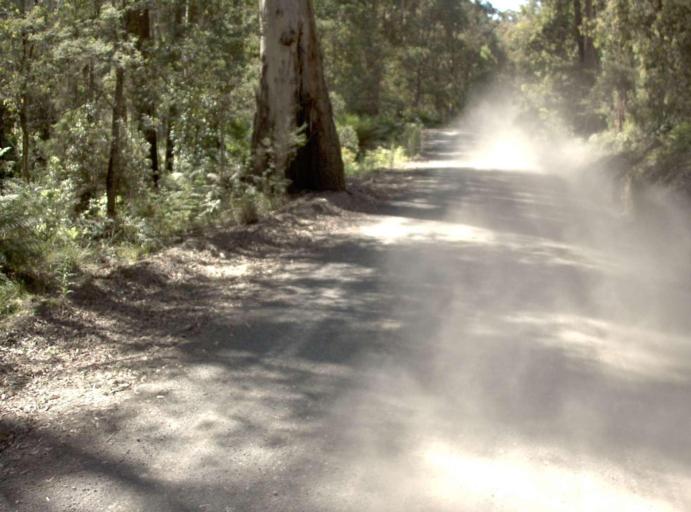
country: AU
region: New South Wales
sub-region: Bombala
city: Bombala
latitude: -37.2103
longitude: 148.7425
